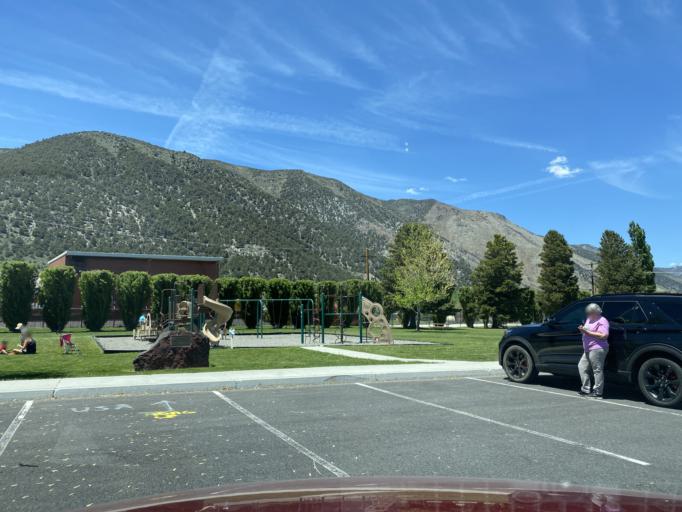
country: US
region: California
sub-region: Mono County
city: Bridgeport
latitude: 37.9595
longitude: -119.1193
